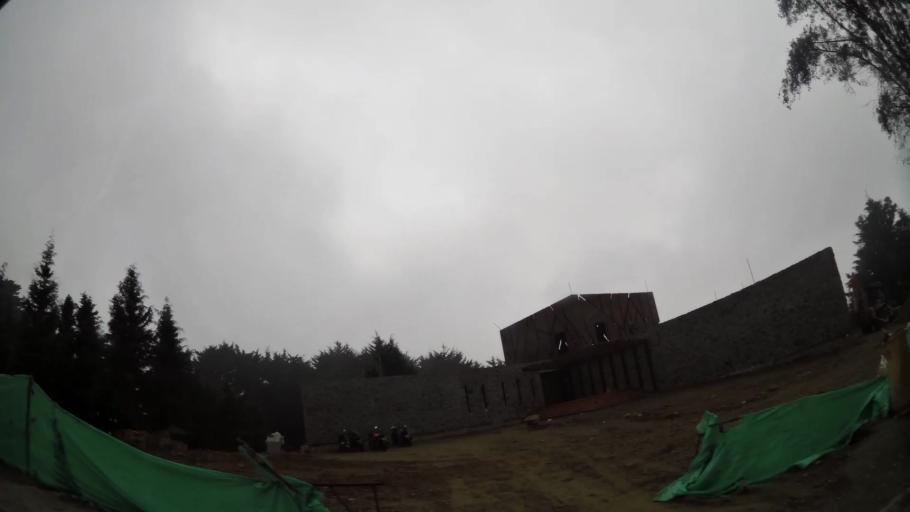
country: CO
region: Antioquia
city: Envigado
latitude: 6.1840
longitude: -75.5474
